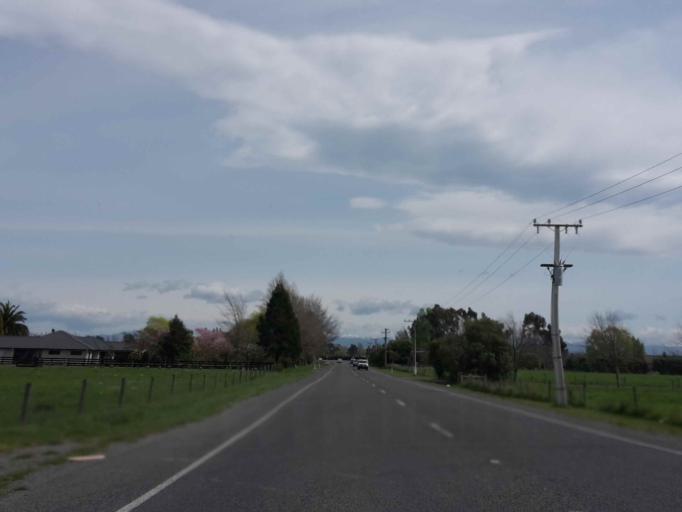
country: NZ
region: Canterbury
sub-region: Waimakariri District
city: Kaiapoi
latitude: -43.3999
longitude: 172.6096
